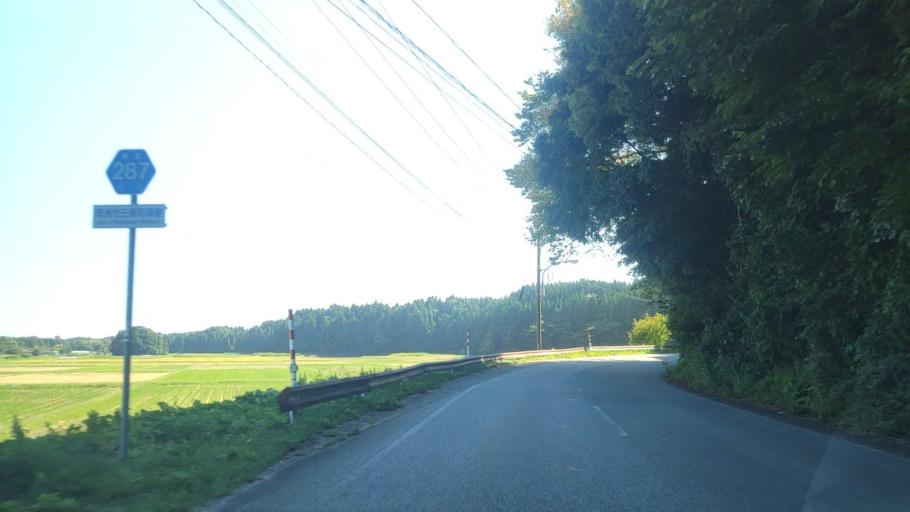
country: JP
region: Ishikawa
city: Nanao
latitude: 37.4783
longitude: 137.3353
